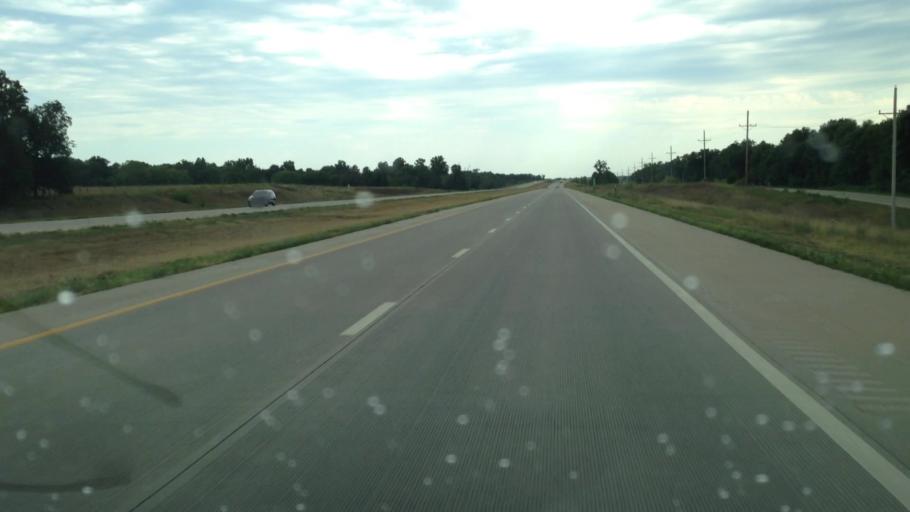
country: US
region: Kansas
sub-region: Douglas County
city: Baldwin City
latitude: 38.7502
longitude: -95.2679
